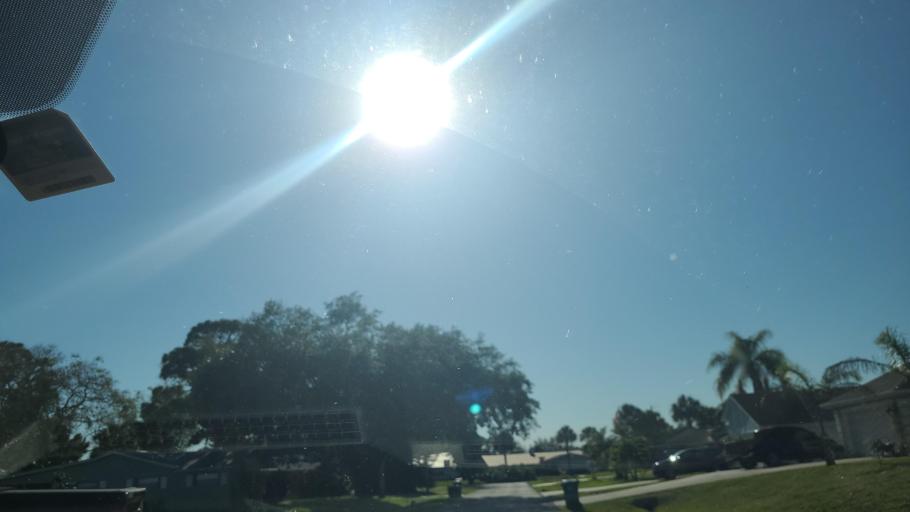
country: US
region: Florida
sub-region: Indian River County
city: Sebastian
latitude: 27.8008
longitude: -80.4921
